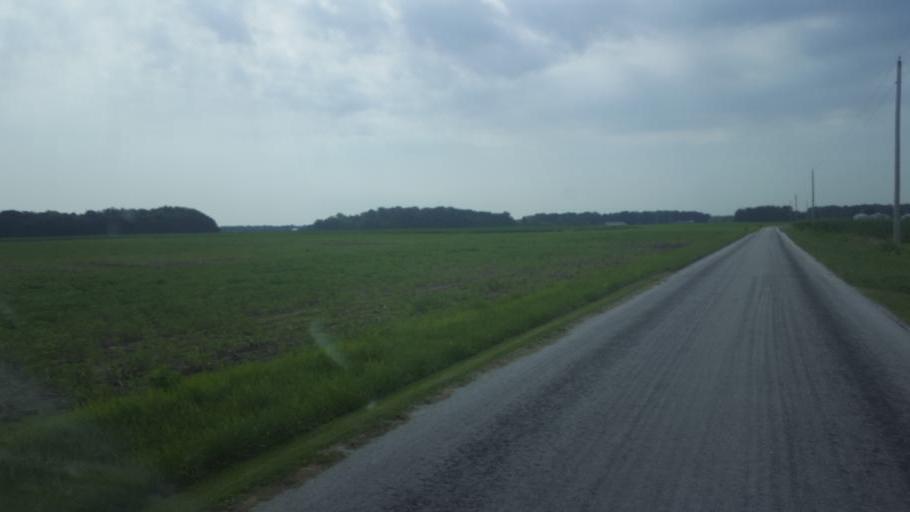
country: US
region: Ohio
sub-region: Hardin County
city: Kenton
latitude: 40.5914
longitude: -83.5220
